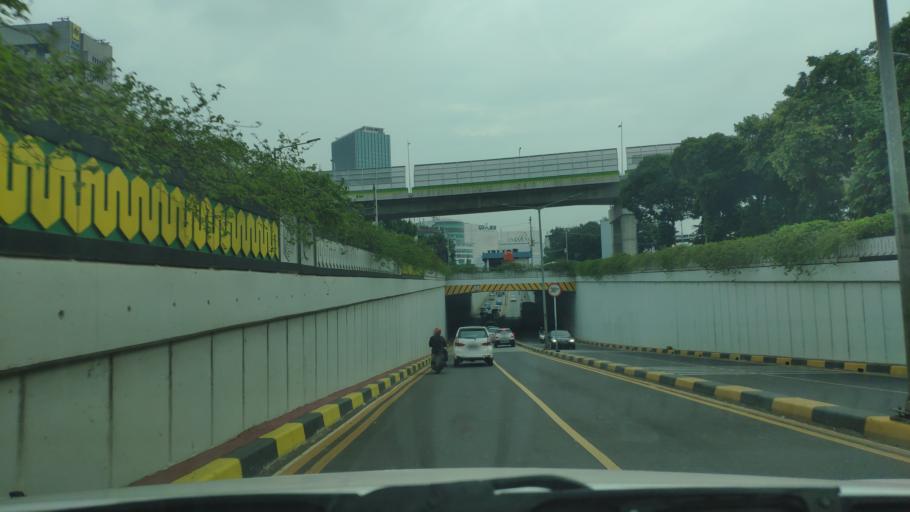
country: ID
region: Jakarta Raya
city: Jakarta
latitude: -6.2388
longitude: 106.8024
